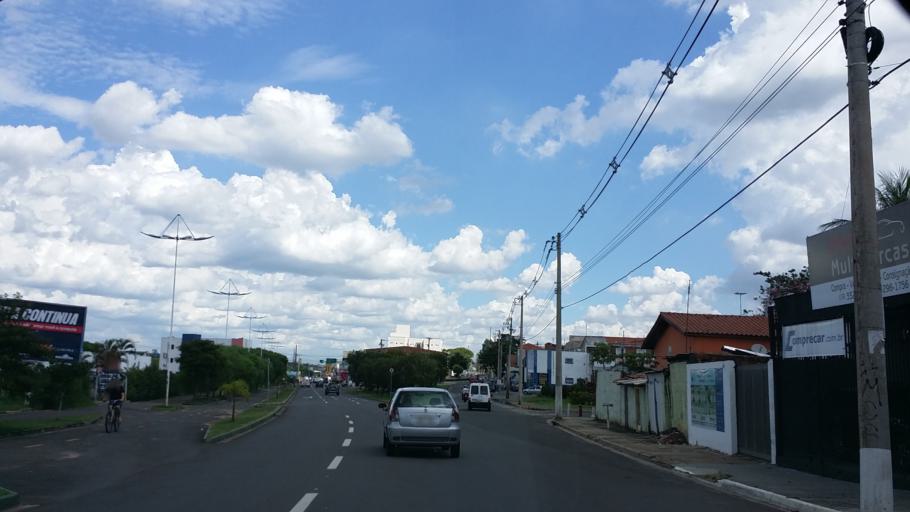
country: BR
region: Sao Paulo
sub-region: Indaiatuba
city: Indaiatuba
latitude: -23.1152
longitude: -47.2332
